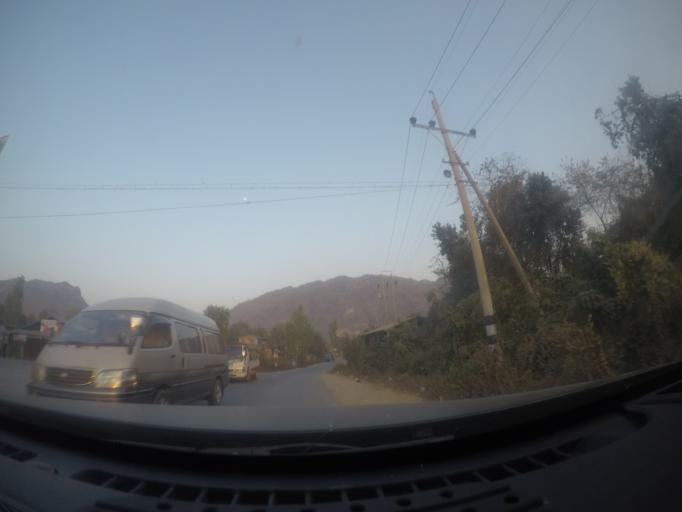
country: MM
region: Mandalay
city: Yamethin
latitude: 20.8175
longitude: 96.3919
